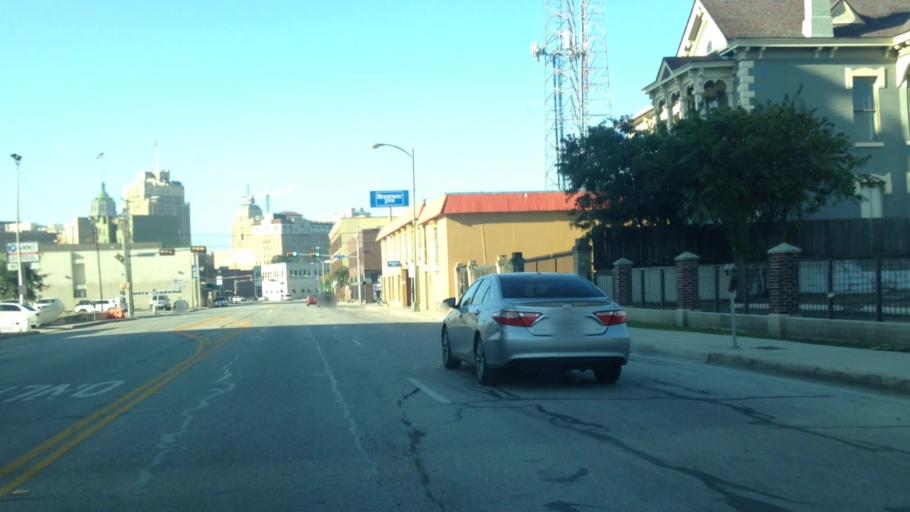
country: US
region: Texas
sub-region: Bexar County
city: San Antonio
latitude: 29.4303
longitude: -98.4853
